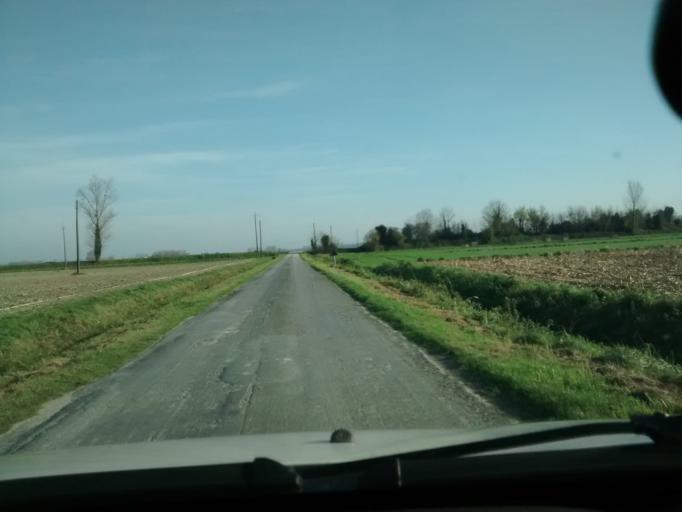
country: FR
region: Brittany
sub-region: Departement d'Ille-et-Vilaine
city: Roz-sur-Couesnon
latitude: 48.6022
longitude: -1.5779
